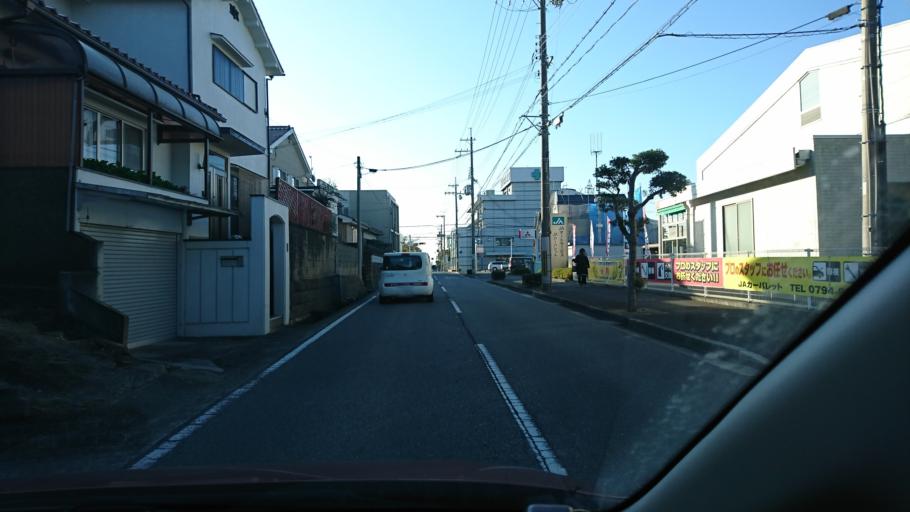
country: JP
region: Hyogo
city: Miki
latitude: 34.7517
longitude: 134.9207
